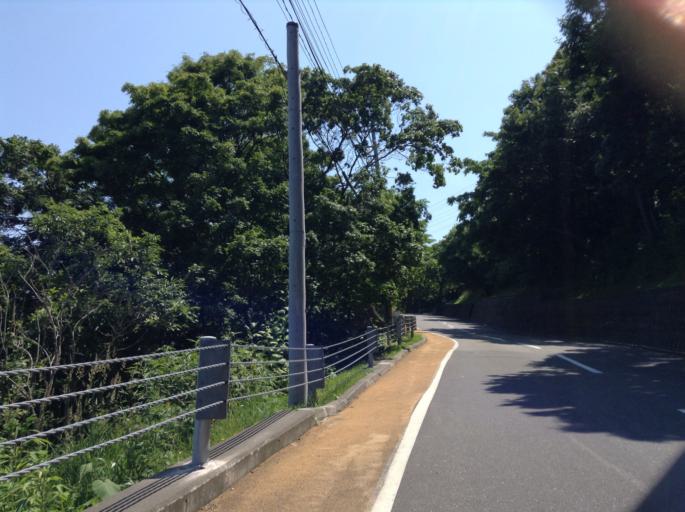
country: JP
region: Hokkaido
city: Wakkanai
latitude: 45.4221
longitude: 141.6701
